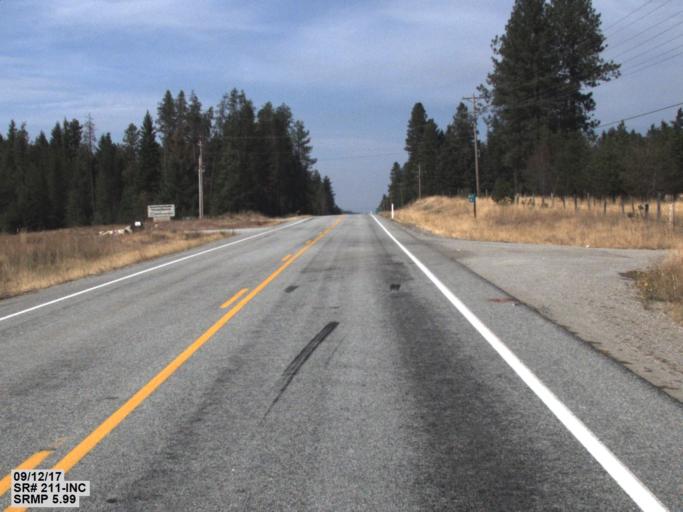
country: US
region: Washington
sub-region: Pend Oreille County
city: Newport
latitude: 48.1759
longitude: -117.3015
